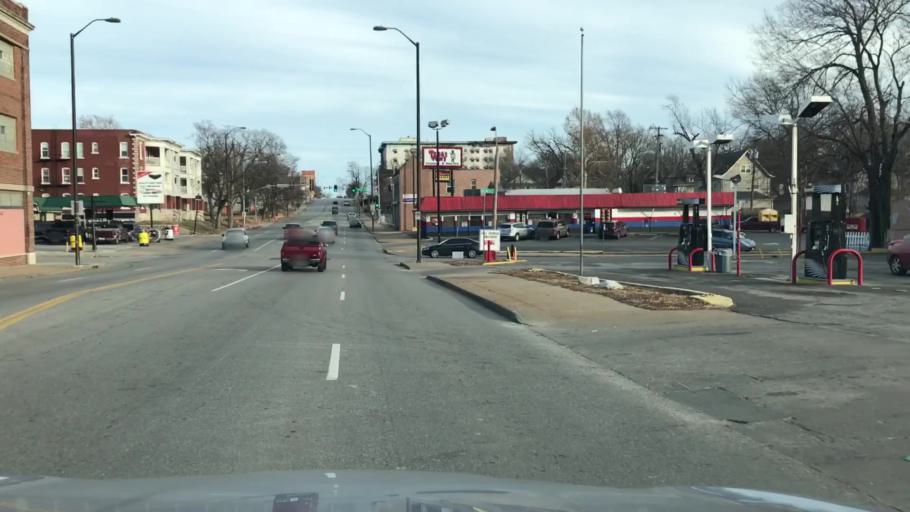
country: US
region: Missouri
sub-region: Jackson County
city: Kansas City
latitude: 39.0689
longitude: -94.5774
